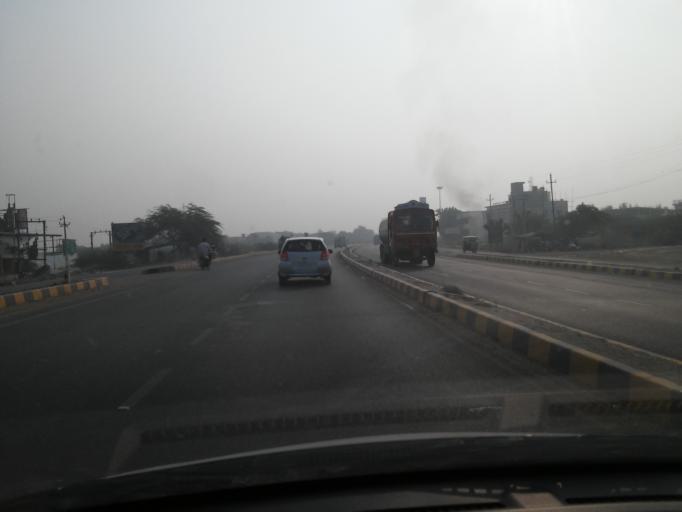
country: IN
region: Gujarat
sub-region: Kachchh
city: Bhuj
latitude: 23.2399
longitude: 69.7180
